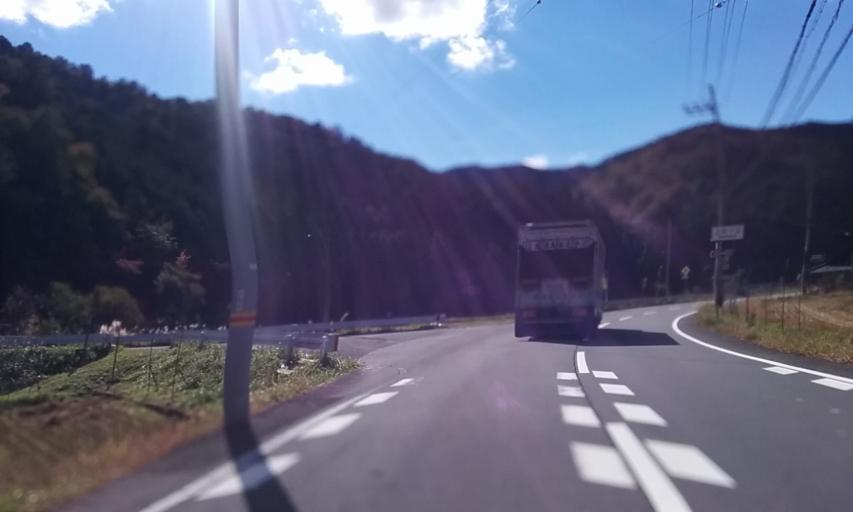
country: JP
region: Kyoto
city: Kameoka
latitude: 35.2062
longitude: 135.5846
